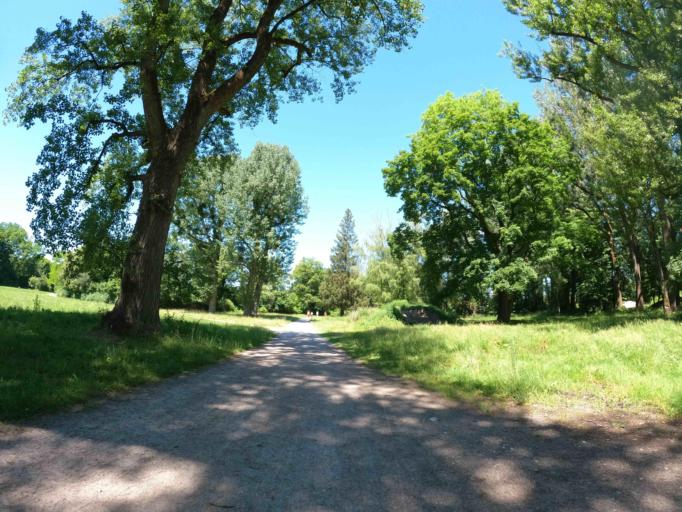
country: DE
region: Bavaria
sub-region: Upper Bavaria
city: Bogenhausen
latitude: 48.1635
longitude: 11.6097
